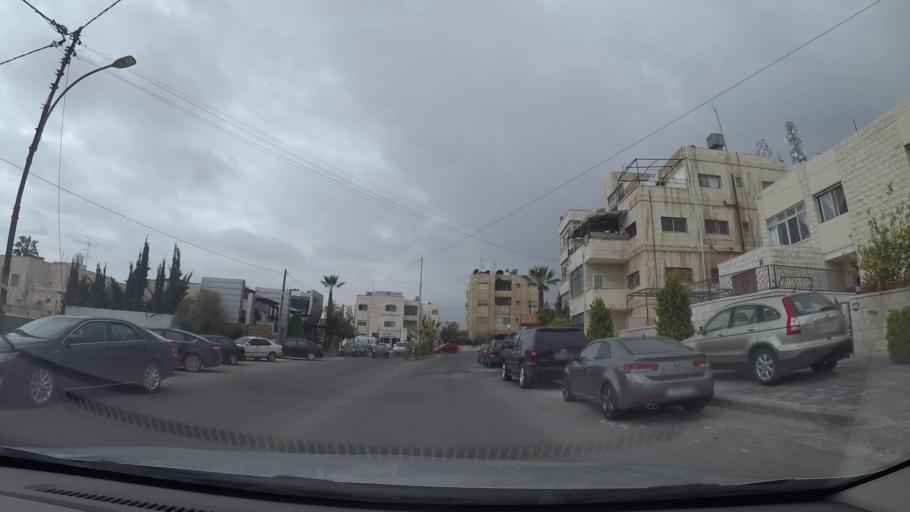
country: JO
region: Amman
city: Wadi as Sir
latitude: 31.9652
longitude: 35.8534
